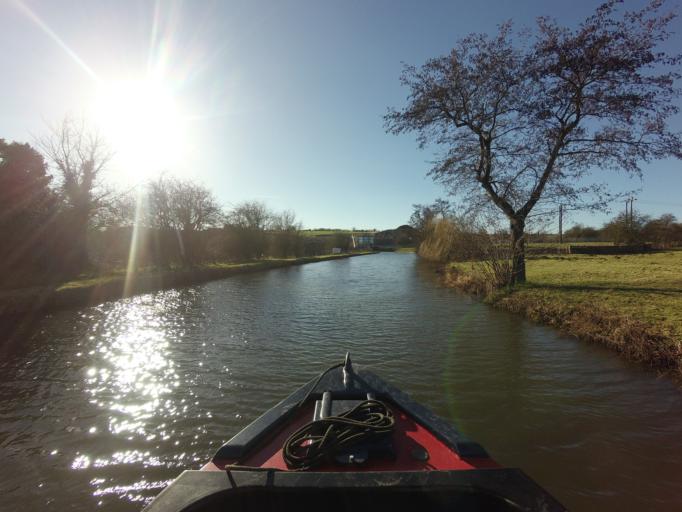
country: GB
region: England
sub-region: Northamptonshire
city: Long Buckby
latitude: 52.2382
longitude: -1.0834
